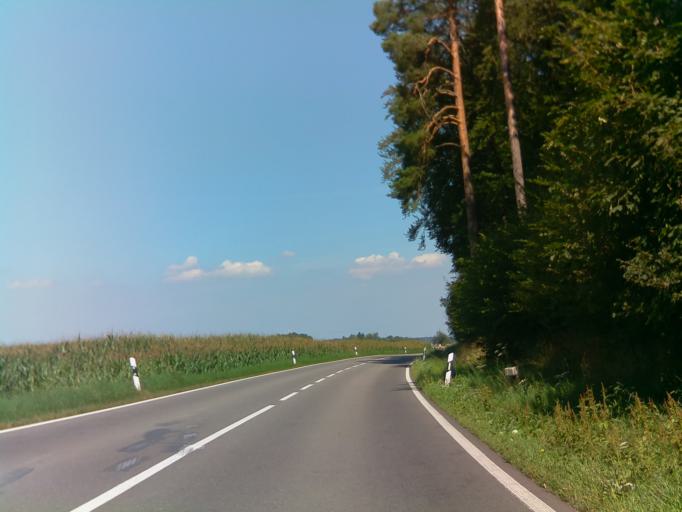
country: DE
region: Baden-Wuerttemberg
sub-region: Regierungsbezirk Stuttgart
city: Rutesheim
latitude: 48.8355
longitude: 8.9710
